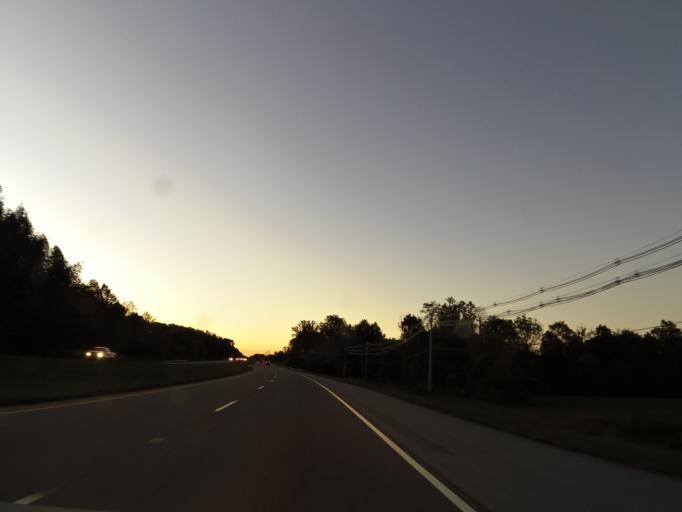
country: US
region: Tennessee
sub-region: Blount County
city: Wildwood
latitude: 35.7496
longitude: -83.8389
